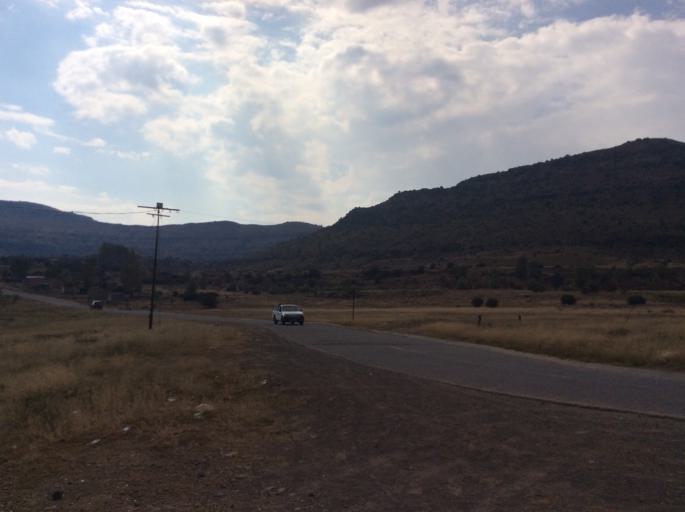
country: LS
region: Mafeteng
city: Mafeteng
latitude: -29.7243
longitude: 27.0368
